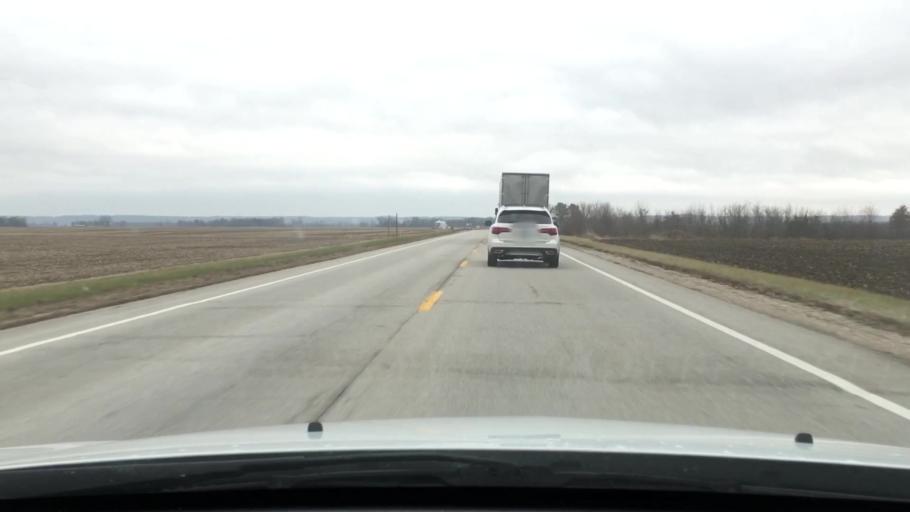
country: US
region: Missouri
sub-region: Pike County
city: Louisiana
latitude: 39.4707
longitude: -91.0247
